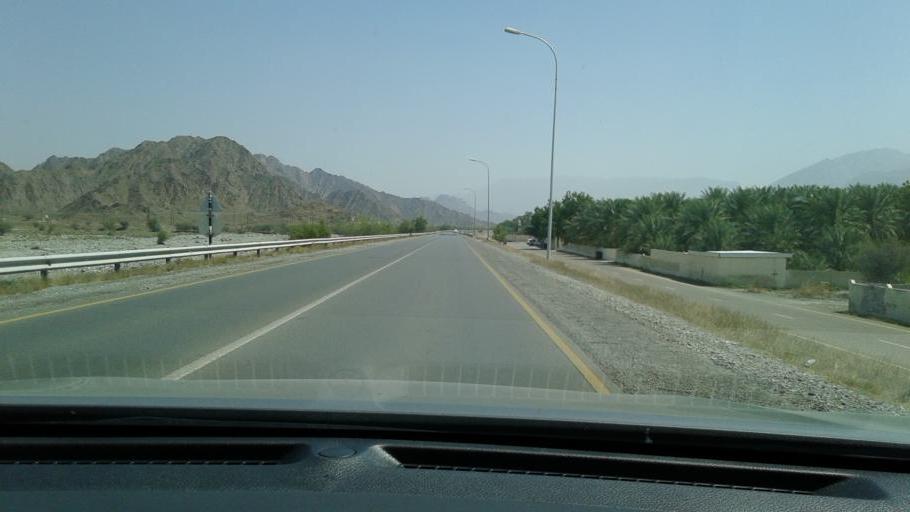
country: OM
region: Al Batinah
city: Rustaq
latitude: 23.3941
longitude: 57.4390
